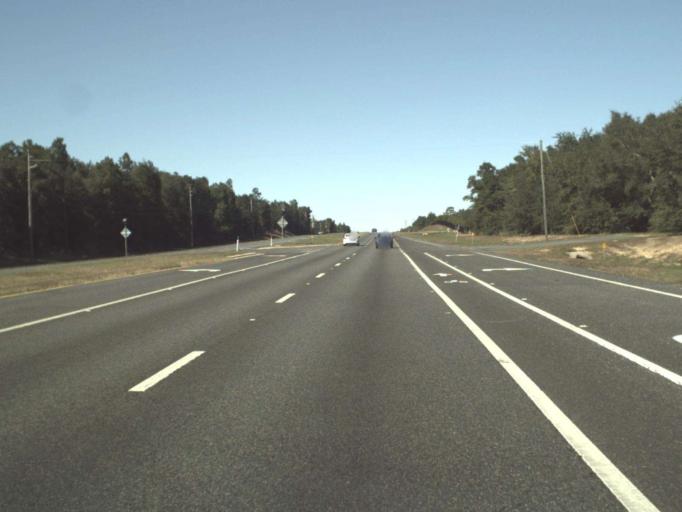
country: US
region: Florida
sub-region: Santa Rosa County
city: East Milton
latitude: 30.5973
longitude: -86.9429
